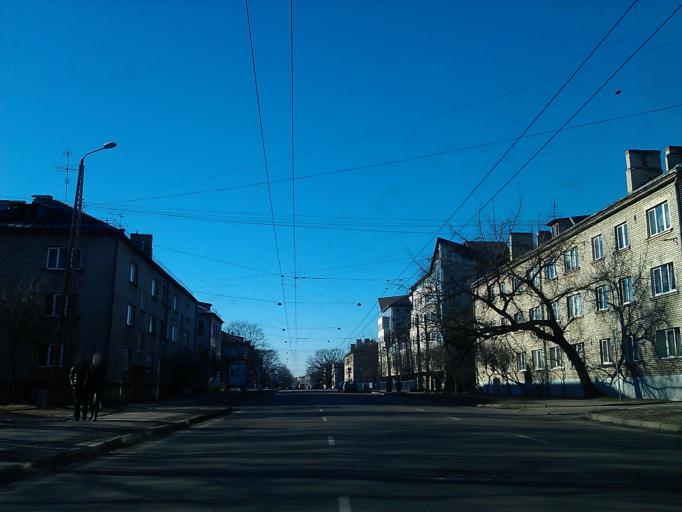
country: LV
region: Riga
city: Riga
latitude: 56.9658
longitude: 24.1743
